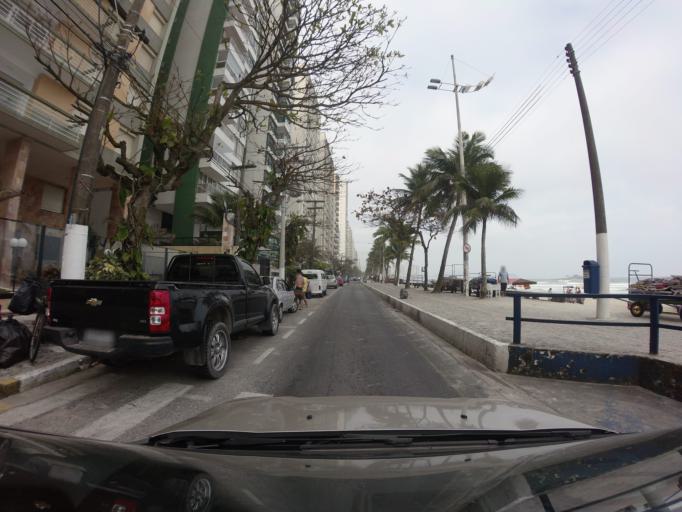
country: BR
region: Sao Paulo
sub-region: Guaruja
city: Guaruja
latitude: -24.0006
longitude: -46.2632
